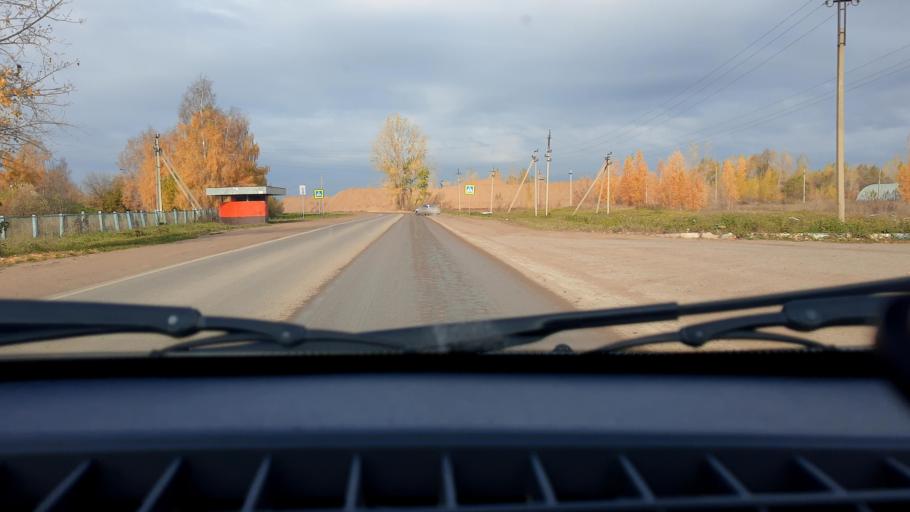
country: RU
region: Bashkortostan
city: Kabakovo
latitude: 54.5477
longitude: 56.1123
